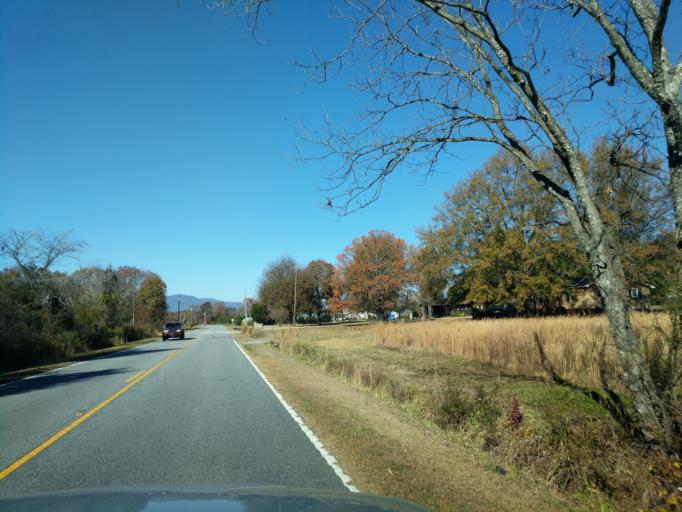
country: US
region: South Carolina
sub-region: Spartanburg County
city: Inman Mills
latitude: 35.0661
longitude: -82.1884
